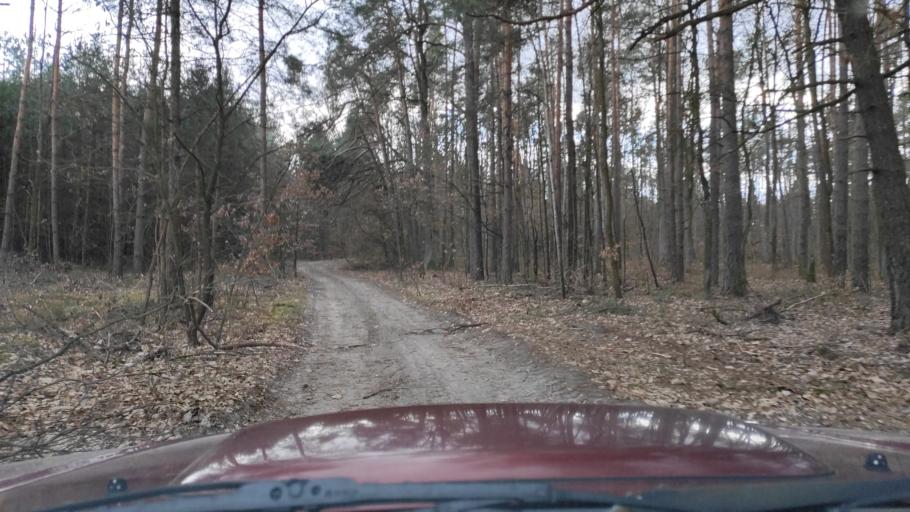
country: PL
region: Masovian Voivodeship
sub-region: Powiat kozienicki
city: Garbatka-Letnisko
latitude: 51.5106
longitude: 21.5630
